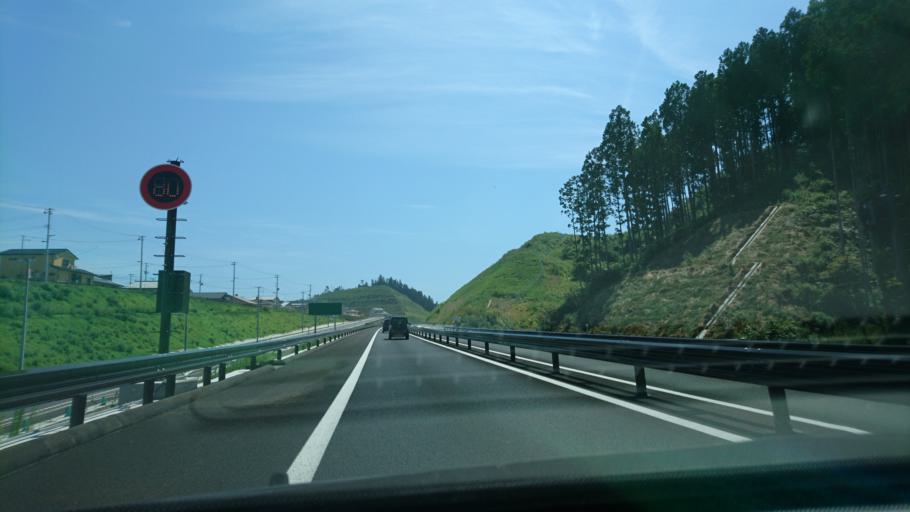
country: JP
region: Iwate
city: Ofunato
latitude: 39.0044
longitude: 141.6129
